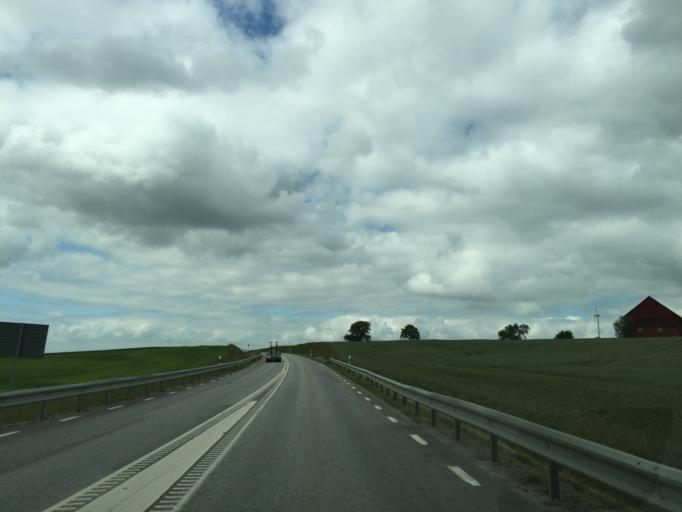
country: SE
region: Skane
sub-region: Svedala Kommun
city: Klagerup
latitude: 55.6198
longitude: 13.2590
